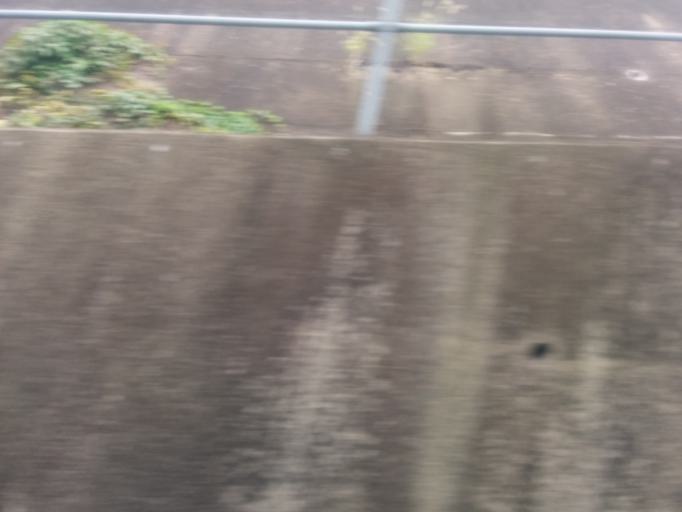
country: JP
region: Kyoto
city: Uji
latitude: 34.9509
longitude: 135.7767
